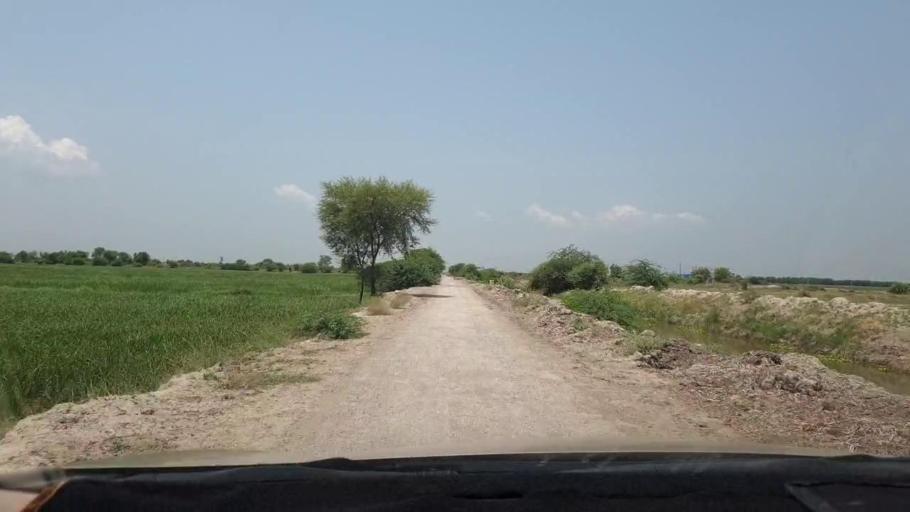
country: PK
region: Sindh
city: Naudero
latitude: 27.6620
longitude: 68.2695
